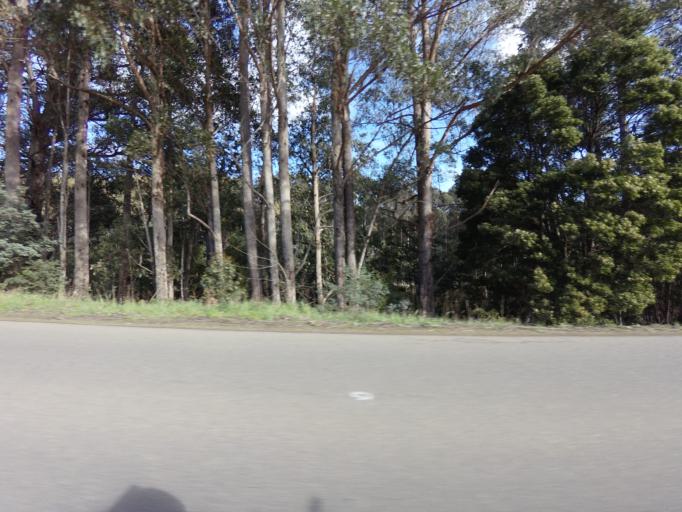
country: AU
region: Tasmania
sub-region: Huon Valley
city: Geeveston
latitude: -43.2203
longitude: 146.9882
